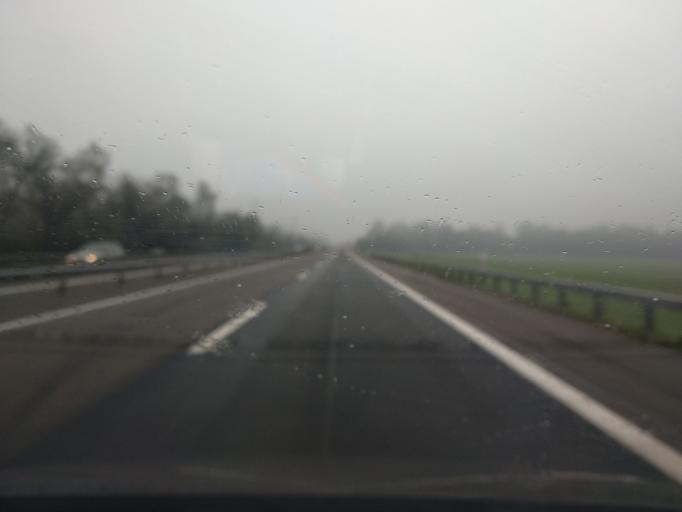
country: CH
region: Saint Gallen
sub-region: Wahlkreis Wil
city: Uzwil
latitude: 47.4556
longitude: 9.1276
